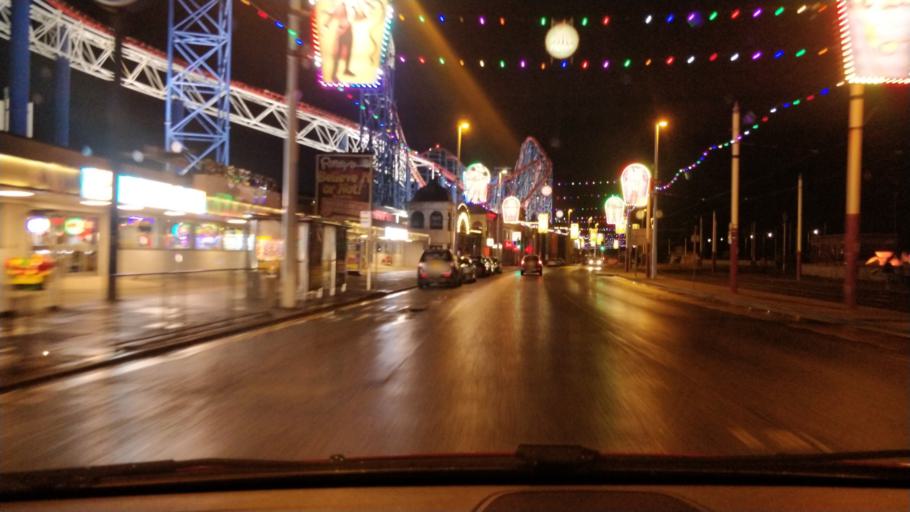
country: GB
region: England
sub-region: Blackpool
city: Blackpool
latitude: 53.7931
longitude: -3.0564
